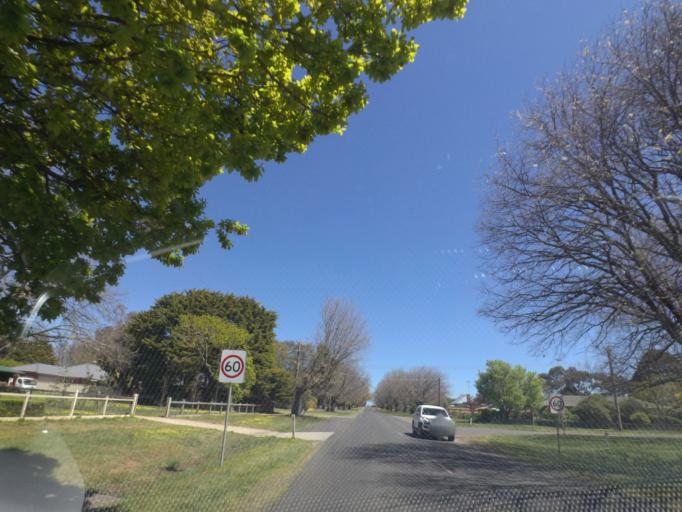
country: AU
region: Victoria
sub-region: Hume
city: Sunbury
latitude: -37.2792
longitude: 144.7278
